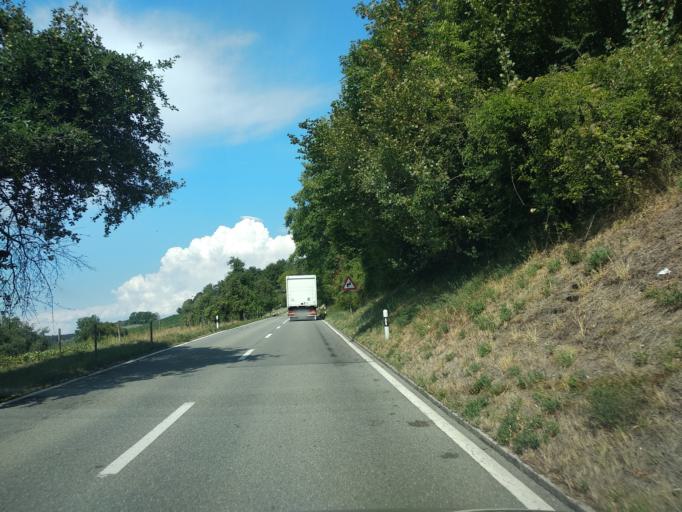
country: CH
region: Zurich
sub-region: Bezirk Winterthur
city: Sulz
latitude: 47.5980
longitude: 8.7789
